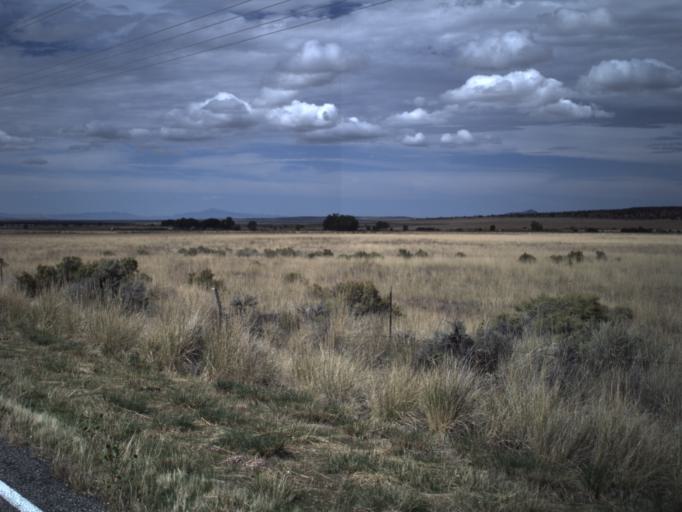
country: US
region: Utah
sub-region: Millard County
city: Fillmore
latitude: 38.9792
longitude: -112.3847
